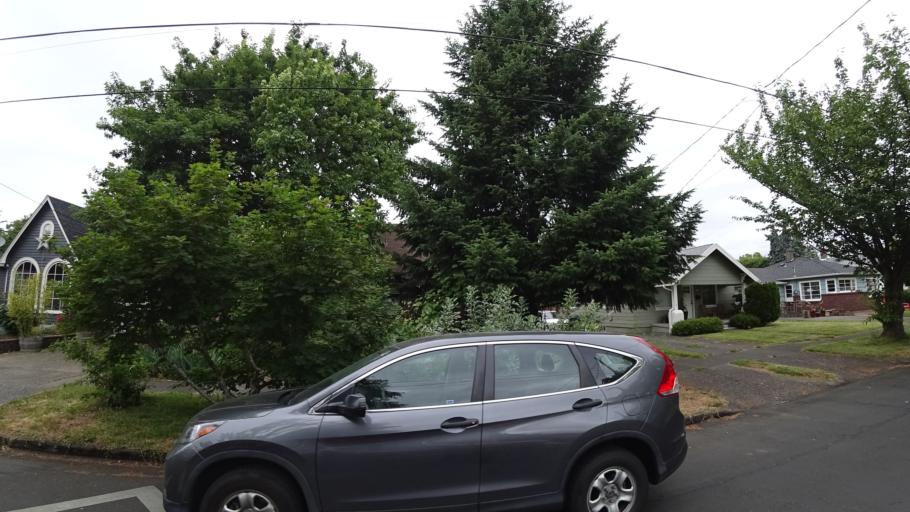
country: US
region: Oregon
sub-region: Multnomah County
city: Portland
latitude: 45.5798
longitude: -122.6985
